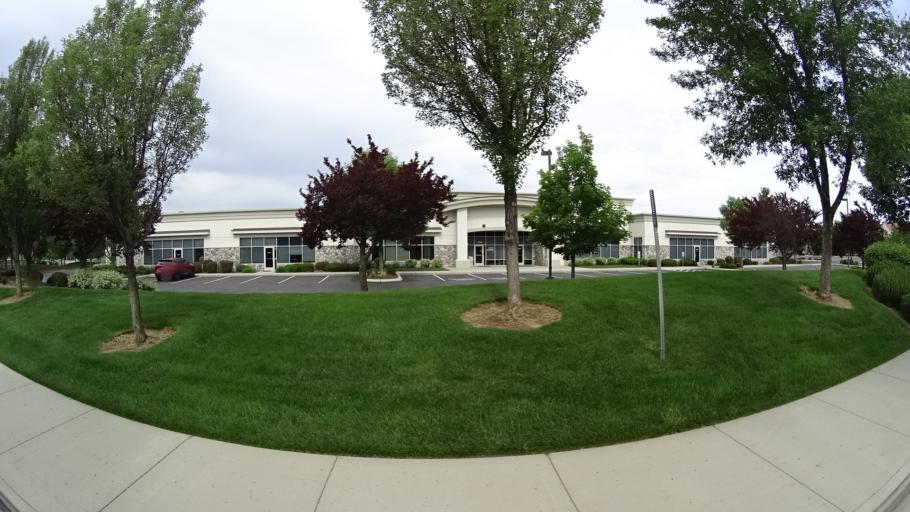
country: US
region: Idaho
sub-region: Ada County
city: Meridian
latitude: 43.5863
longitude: -116.3518
